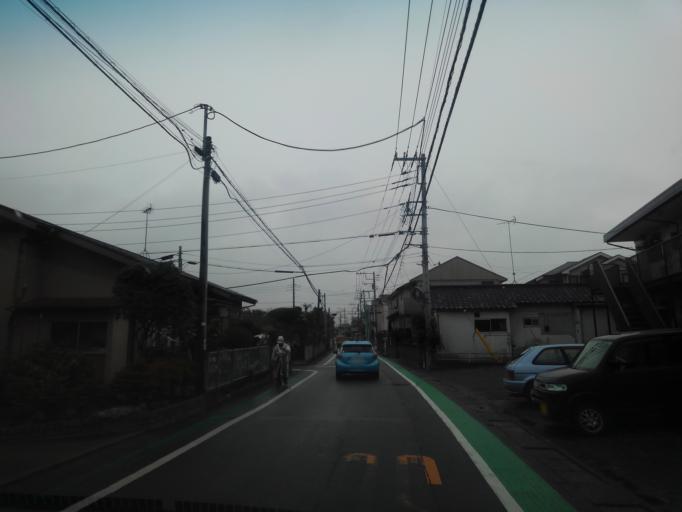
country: JP
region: Tokyo
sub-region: Machida-shi
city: Machida
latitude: 35.5839
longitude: 139.3901
